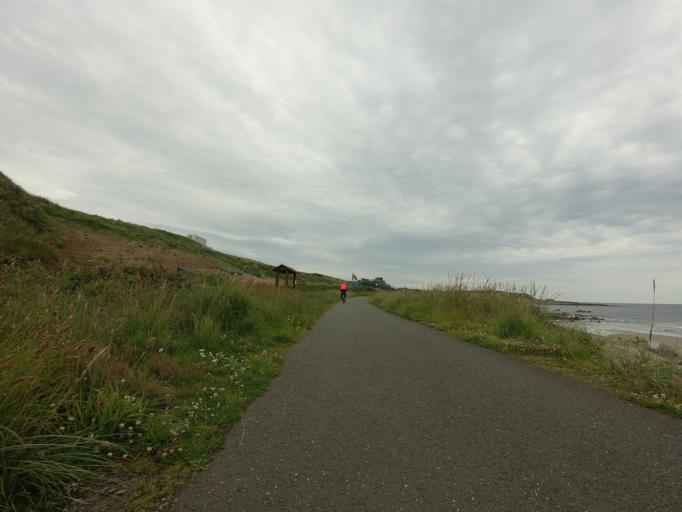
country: GB
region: Scotland
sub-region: Aberdeenshire
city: Whitehills
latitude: 57.6731
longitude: -2.5634
